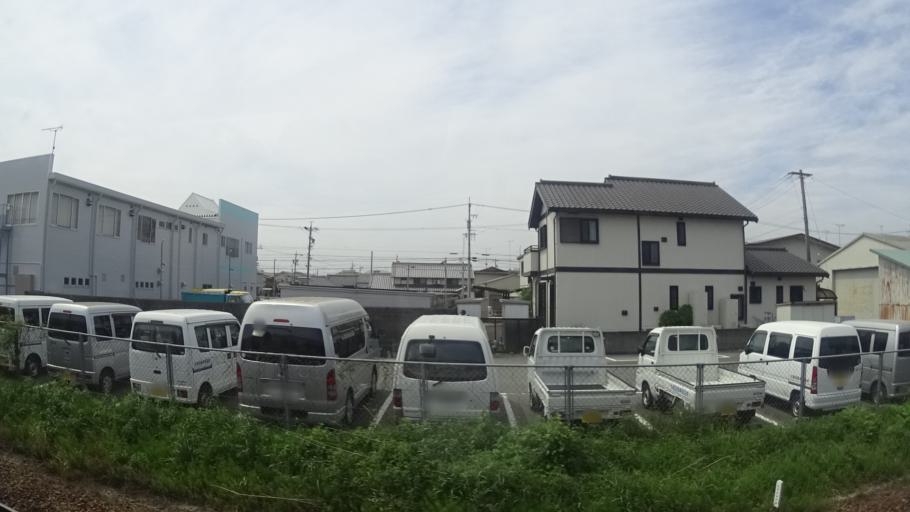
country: JP
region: Mie
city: Hisai-motomachi
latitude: 34.5832
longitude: 136.5284
